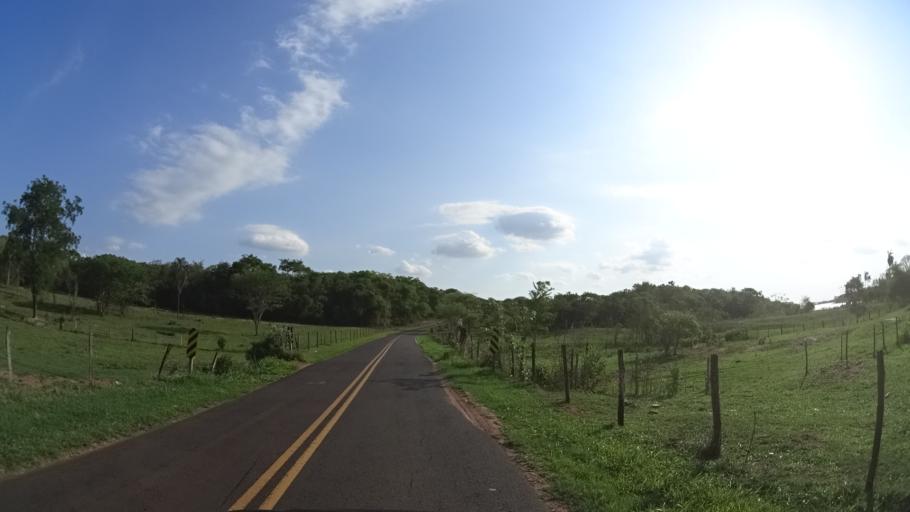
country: BR
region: Sao Paulo
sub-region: Urupes
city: Urupes
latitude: -21.4019
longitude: -49.5168
